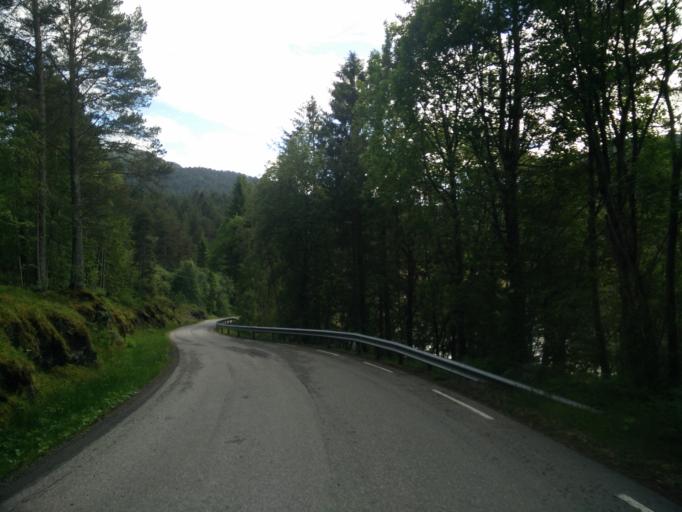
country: NO
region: More og Romsdal
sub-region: Kristiansund
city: Rensvik
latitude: 63.0202
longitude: 7.9595
